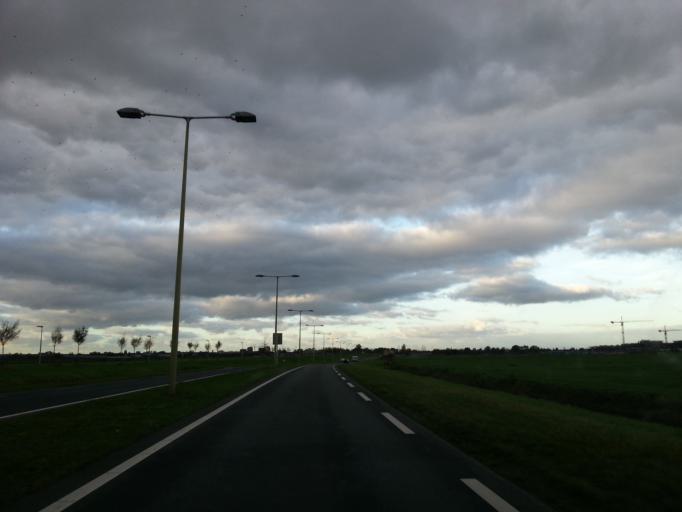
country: NL
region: South Holland
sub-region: Gemeente Lansingerland
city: Berkel en Rodenrijs
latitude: 51.9832
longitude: 4.4478
